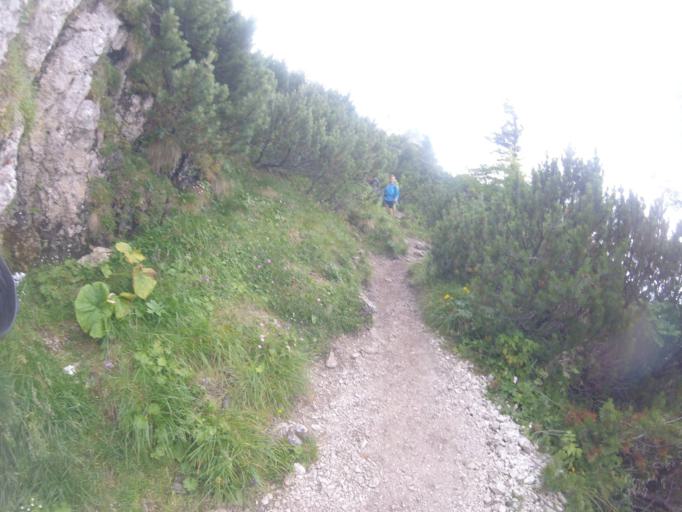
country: SK
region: Zilinsky
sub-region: Okres Zilina
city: Terchova
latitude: 49.2342
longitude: 19.1032
